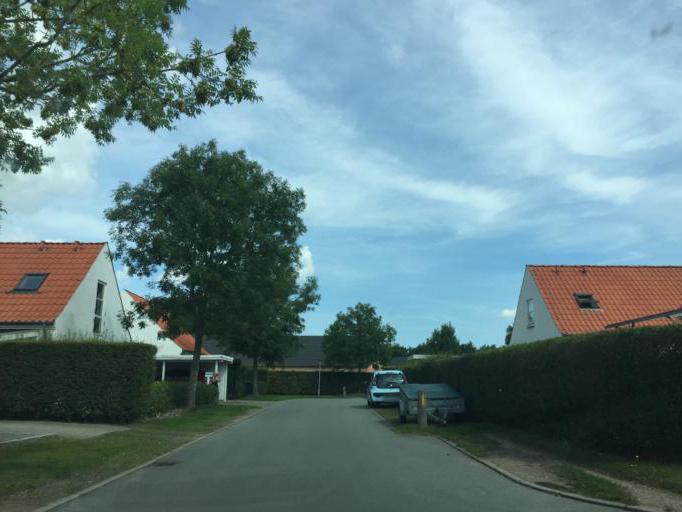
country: DK
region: South Denmark
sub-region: Odense Kommune
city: Hojby
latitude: 55.3379
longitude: 10.4421
